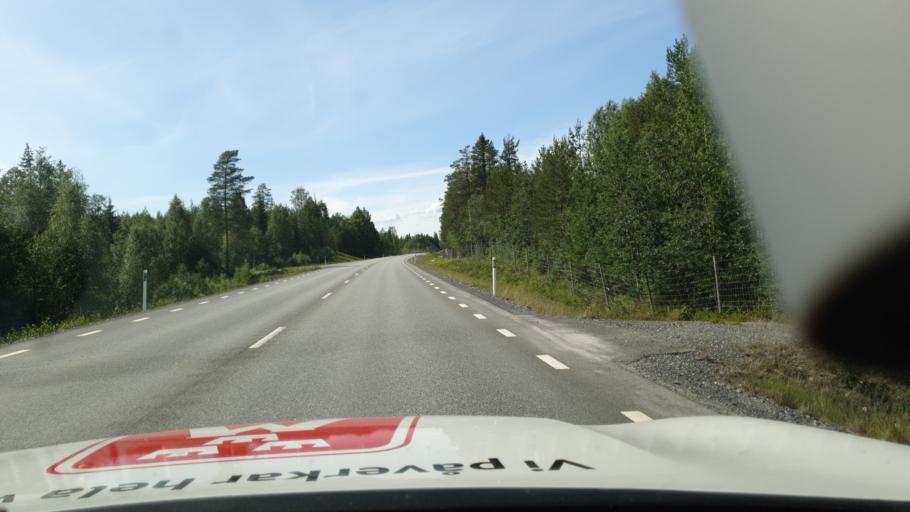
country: SE
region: Vaesterbotten
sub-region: Skelleftea Kommun
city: Forsbacka
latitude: 64.8298
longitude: 20.5532
